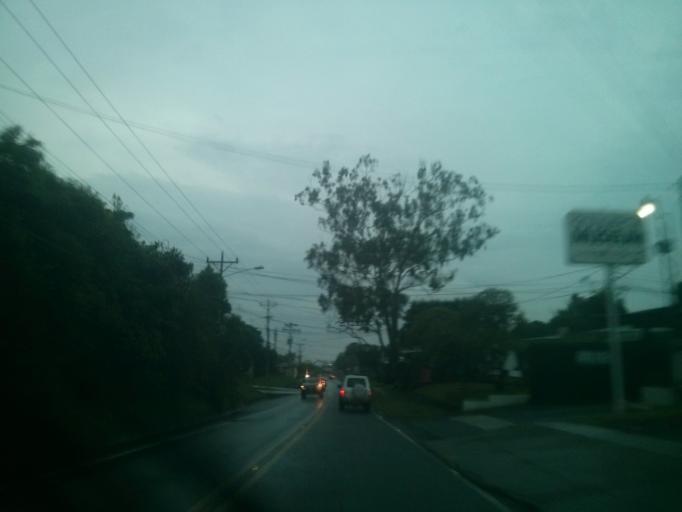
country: CR
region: Alajuela
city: Alajuela
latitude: 10.0341
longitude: -84.2127
